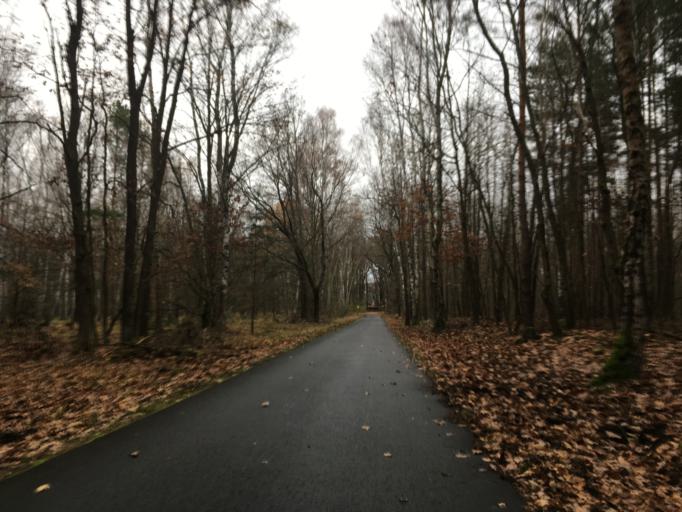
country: DE
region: Brandenburg
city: Mullrose
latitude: 52.2404
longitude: 14.4498
